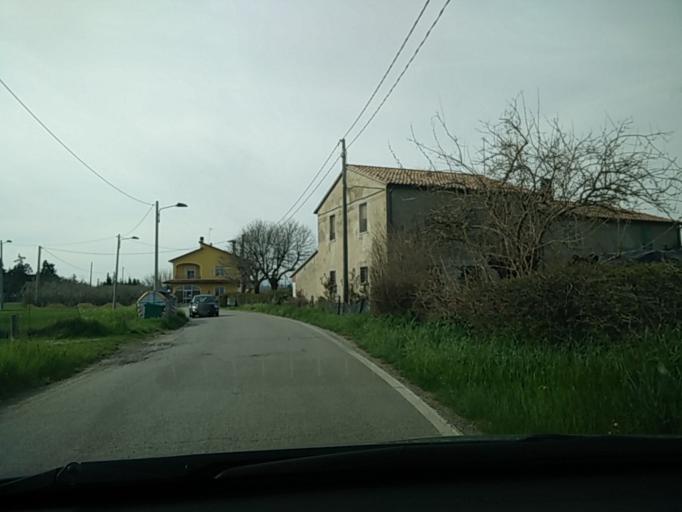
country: IT
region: Emilia-Romagna
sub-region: Provincia di Rimini
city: Santa Giustina
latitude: 44.0765
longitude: 12.5061
